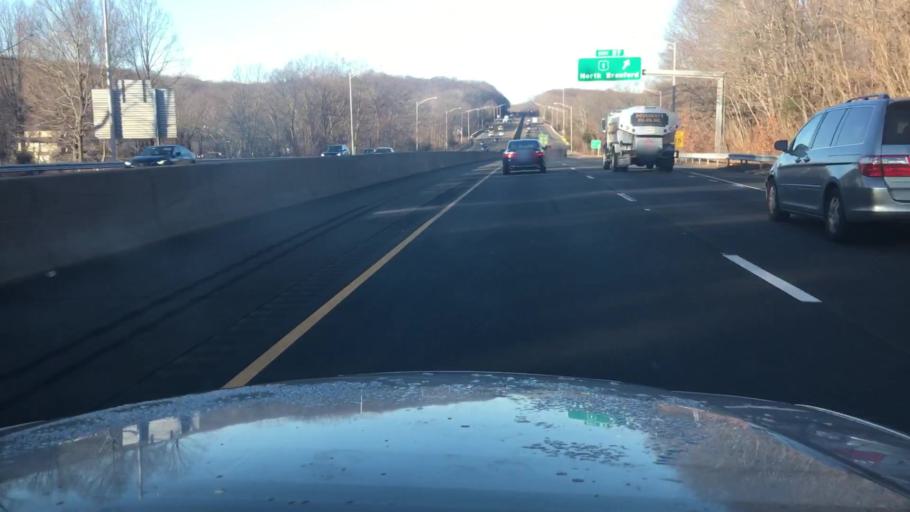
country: US
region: Connecticut
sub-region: New Haven County
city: Guilford
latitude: 41.2965
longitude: -72.6989
